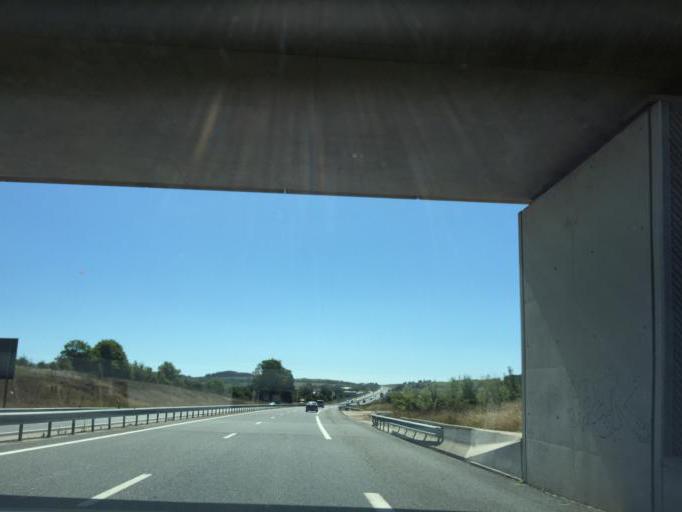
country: FR
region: Midi-Pyrenees
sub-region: Departement de l'Aveyron
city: La Cavalerie
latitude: 43.9950
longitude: 3.1716
